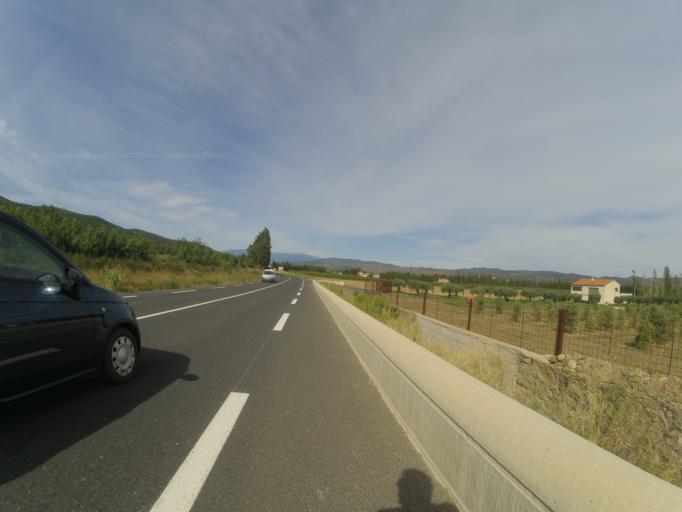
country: FR
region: Languedoc-Roussillon
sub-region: Departement des Pyrenees-Orientales
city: Ille-sur-Tet
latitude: 42.6584
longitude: 2.6470
